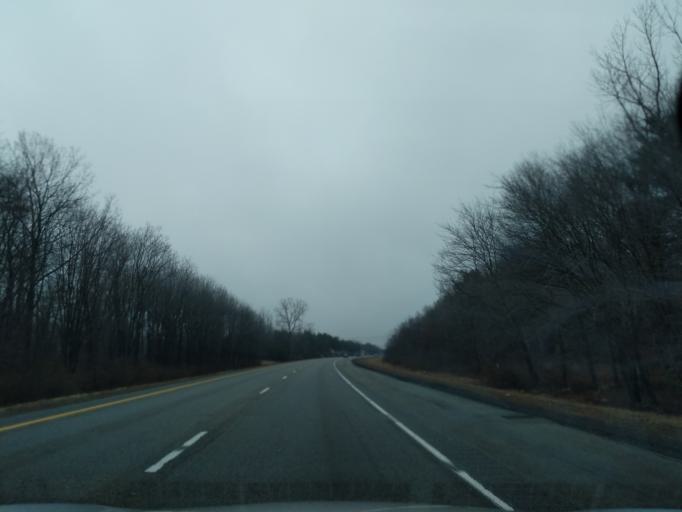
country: US
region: Massachusetts
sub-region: Worcester County
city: Auburn
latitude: 42.1649
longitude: -71.8459
